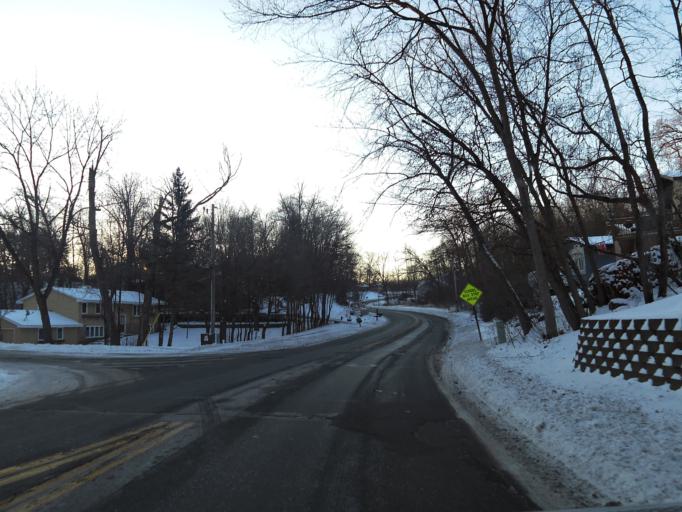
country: US
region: Minnesota
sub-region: Scott County
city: Prior Lake
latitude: 44.7246
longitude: -93.4025
